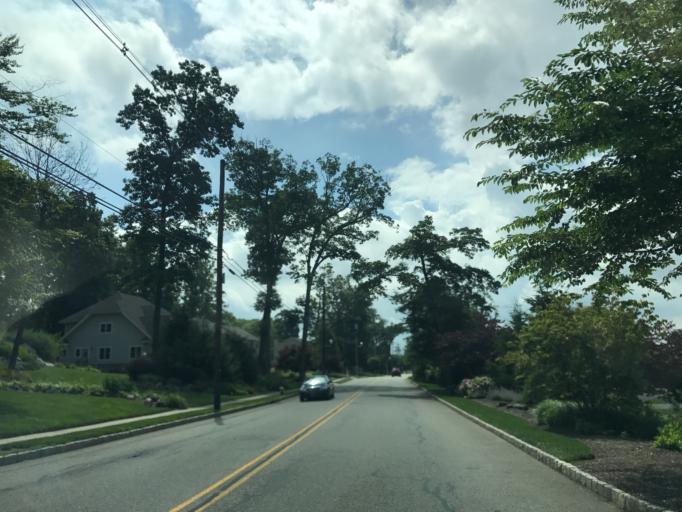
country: US
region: New Jersey
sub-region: Morris County
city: Mountain Lakes
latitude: 40.8992
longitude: -74.4204
